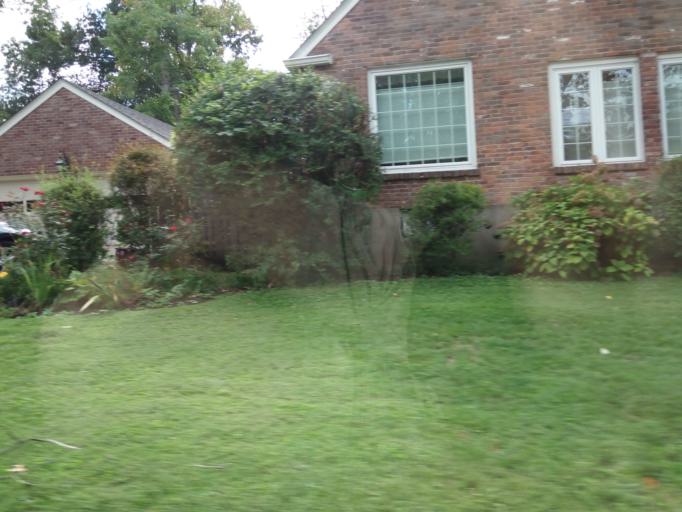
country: US
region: Kentucky
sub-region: Jefferson County
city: Audubon Park
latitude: 38.2057
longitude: -85.7272
